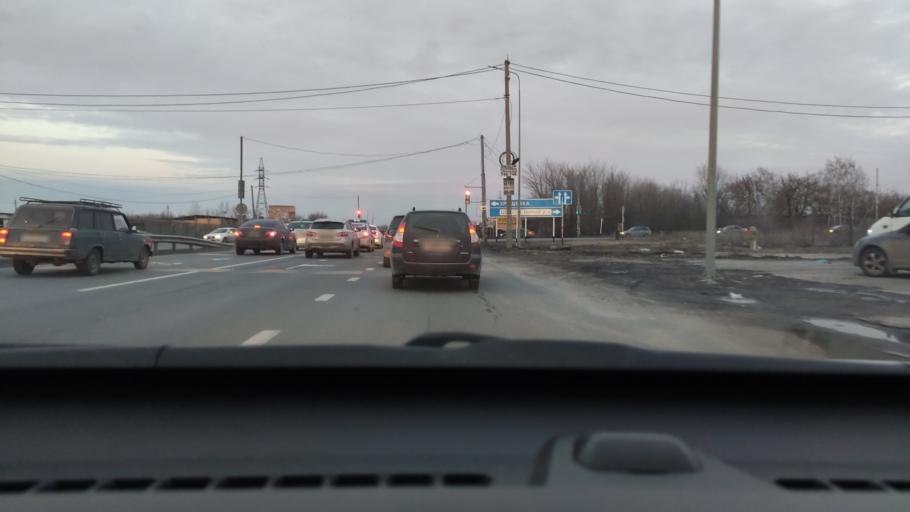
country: RU
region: Samara
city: Tol'yatti
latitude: 53.5538
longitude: 49.3612
